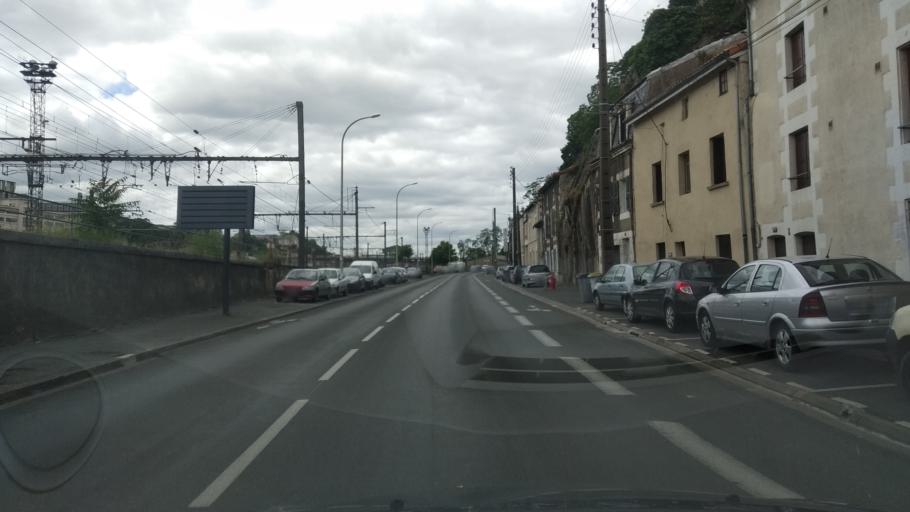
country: FR
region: Poitou-Charentes
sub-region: Departement de la Vienne
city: Poitiers
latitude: 46.5892
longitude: 0.3385
